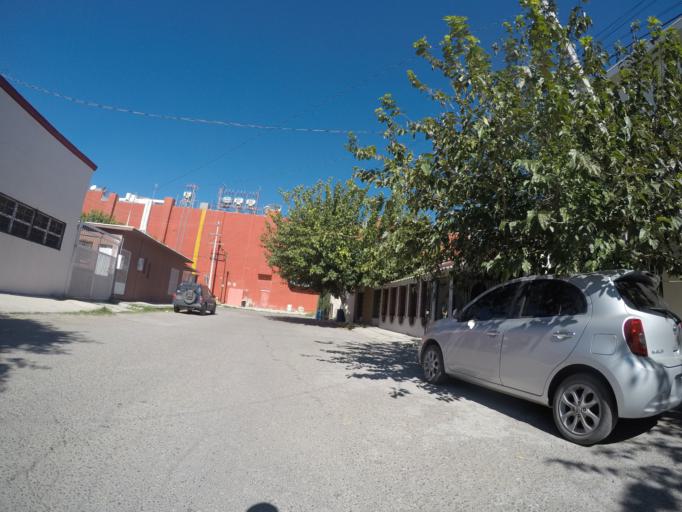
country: MX
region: Chihuahua
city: Ciudad Juarez
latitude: 31.7214
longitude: -106.4189
